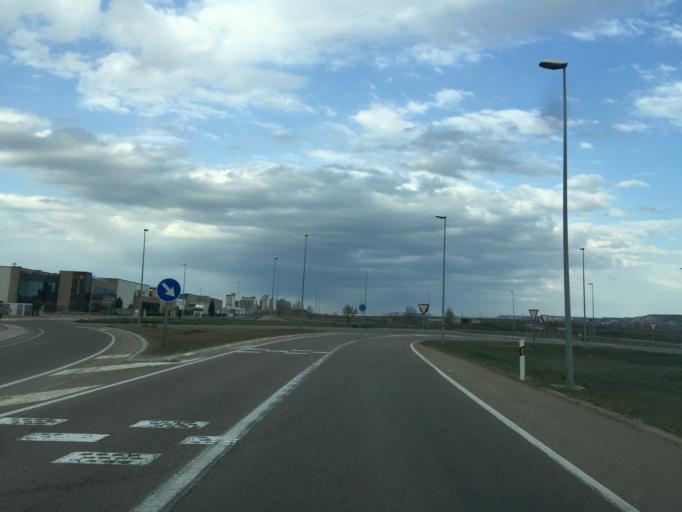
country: ES
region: Castille and Leon
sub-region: Provincia de Palencia
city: Venta de Banos
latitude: 41.9299
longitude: -4.4848
